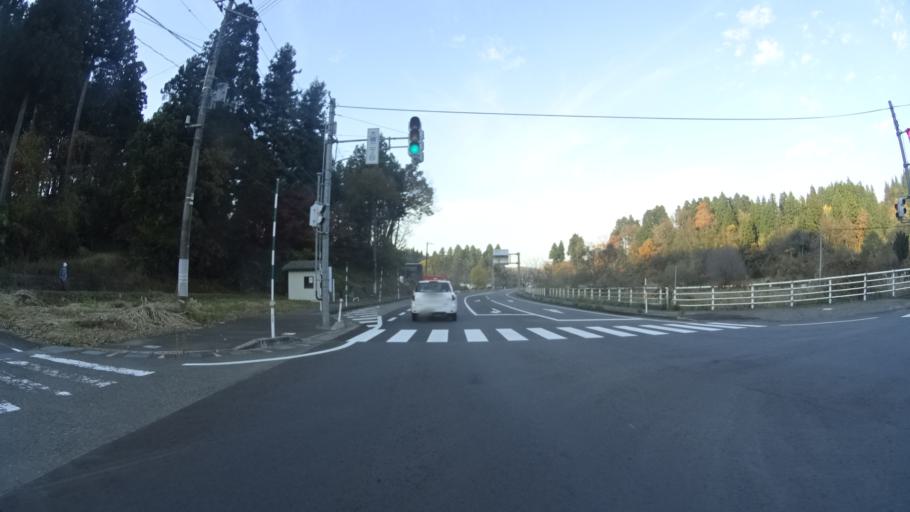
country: JP
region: Niigata
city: Nagaoka
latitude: 37.4263
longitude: 138.7261
